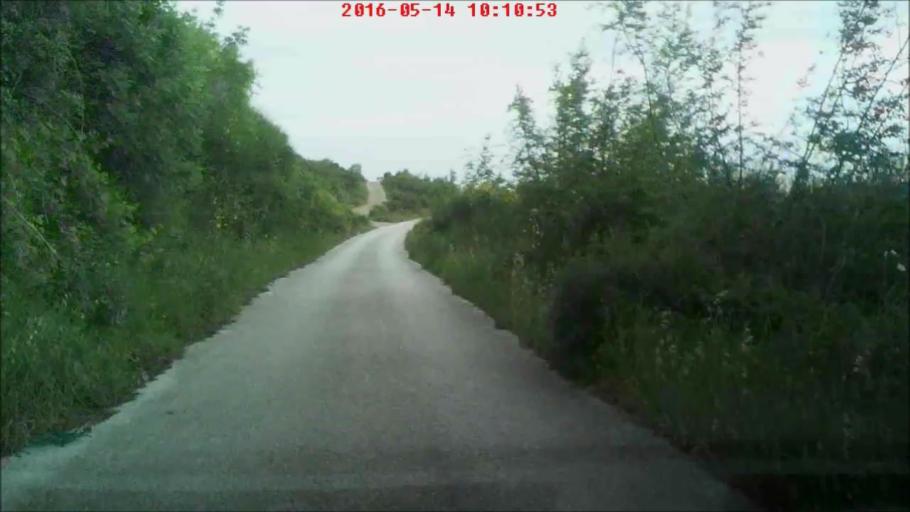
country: HR
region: Dubrovacko-Neretvanska
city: Podgora
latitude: 42.7380
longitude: 17.9414
